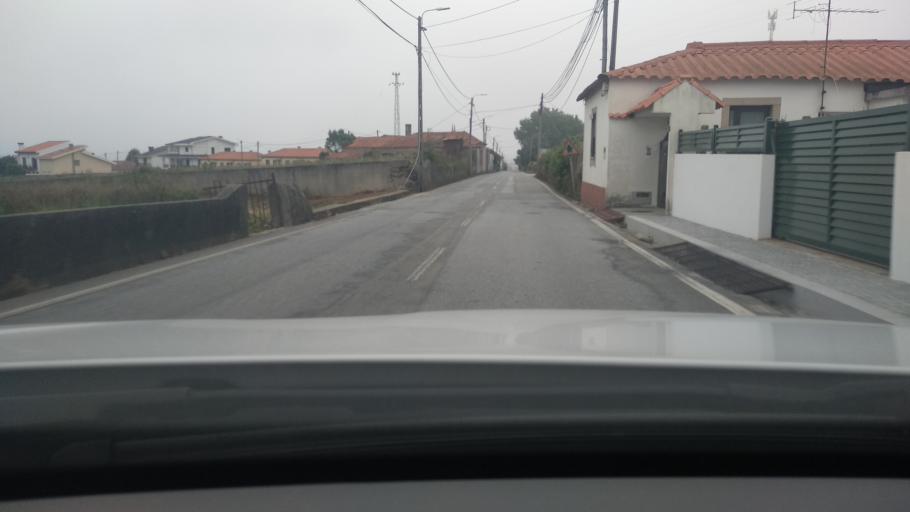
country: PT
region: Aveiro
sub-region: Espinho
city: Souto
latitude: 40.9864
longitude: -8.6245
